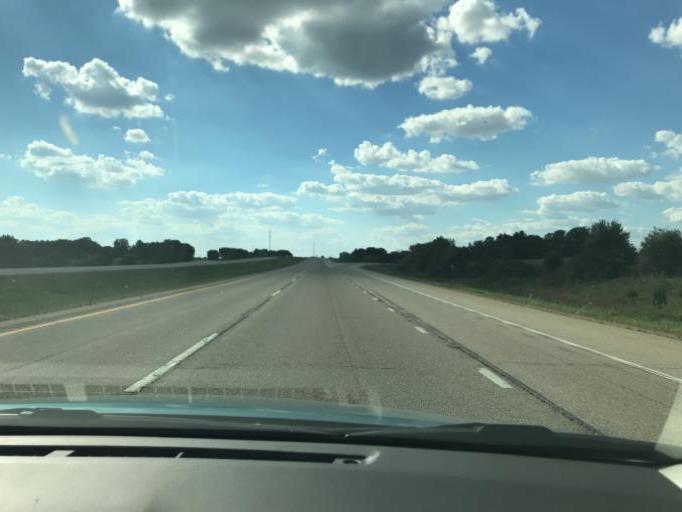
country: US
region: Wisconsin
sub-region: Rock County
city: Clinton
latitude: 42.5727
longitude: -88.8578
